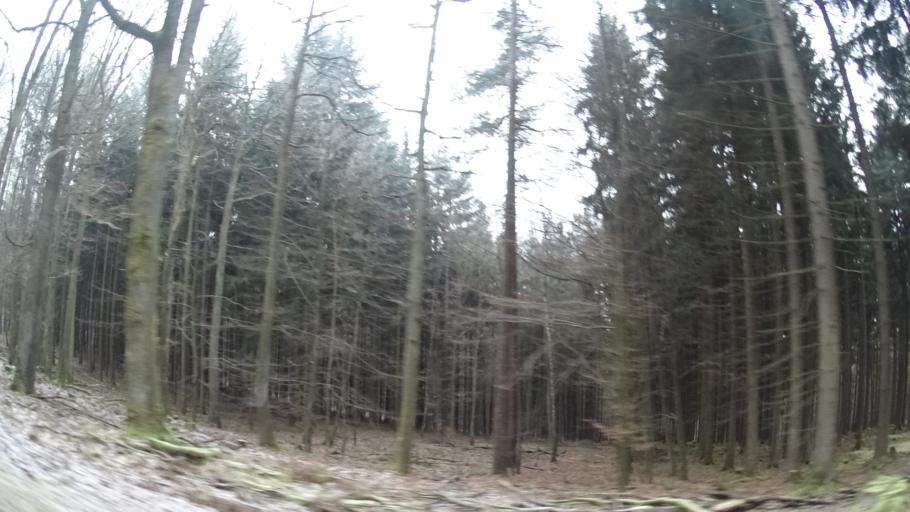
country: DE
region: Hesse
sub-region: Regierungsbezirk Darmstadt
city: Bad Orb
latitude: 50.1956
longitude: 9.4136
